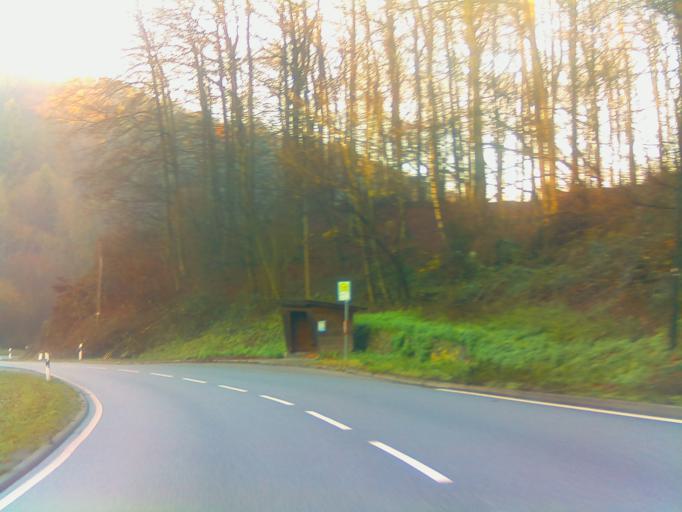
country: DE
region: Hesse
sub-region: Regierungsbezirk Darmstadt
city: Furth
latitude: 49.6640
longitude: 8.8272
